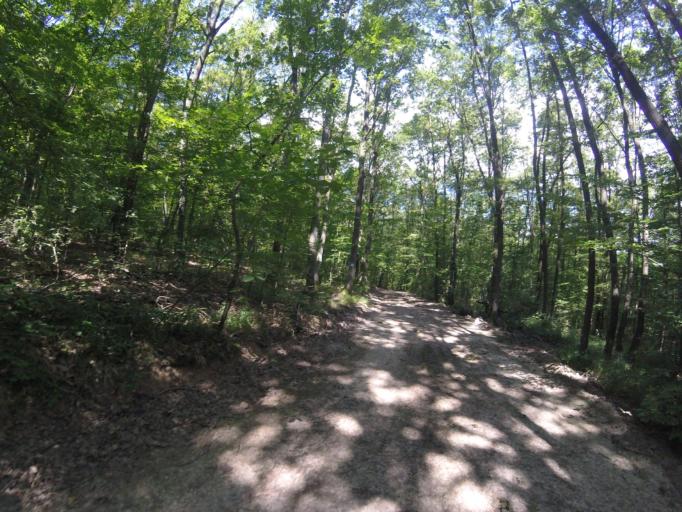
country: HU
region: Nograd
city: Romhany
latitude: 47.8962
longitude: 19.2442
